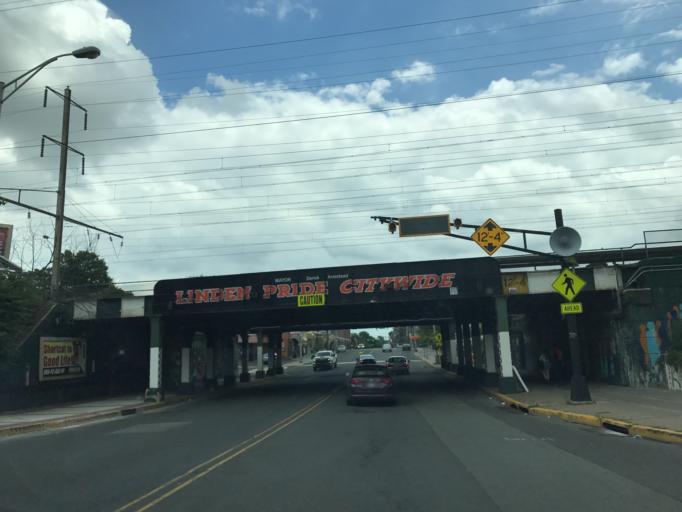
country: US
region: New Jersey
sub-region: Union County
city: Linden
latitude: 40.6303
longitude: -74.2516
